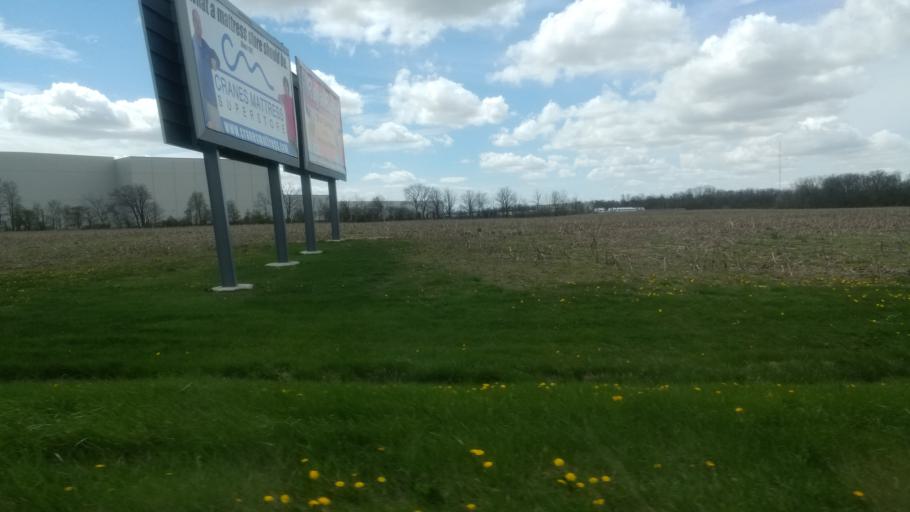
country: US
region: Ohio
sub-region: Hancock County
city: Findlay
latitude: 41.0827
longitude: -83.6327
